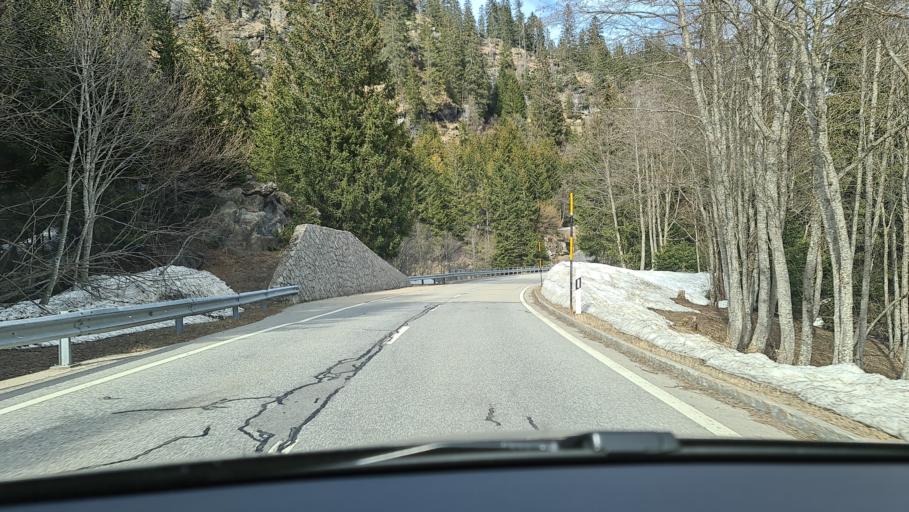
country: CH
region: Ticino
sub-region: Blenio District
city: Cancori
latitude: 46.5215
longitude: 8.8846
